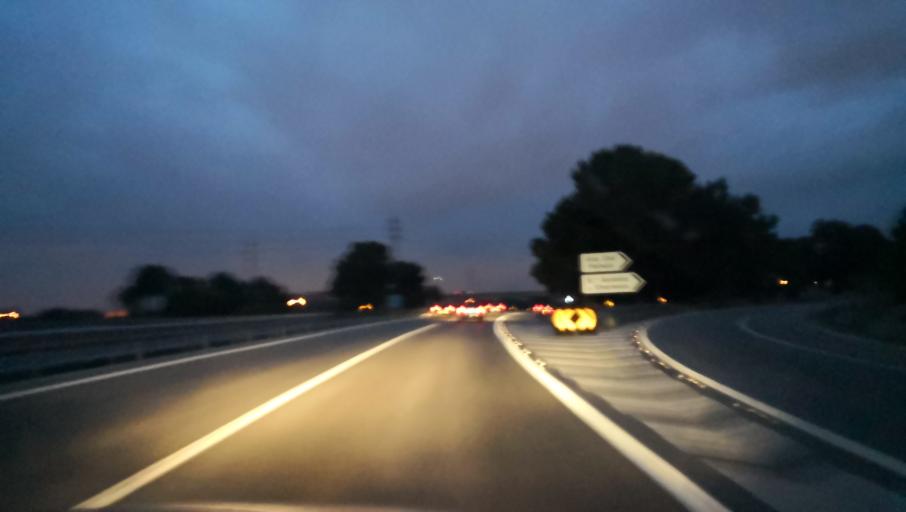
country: PT
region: Setubal
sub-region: Barreiro
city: Santo Antonio da Charneca
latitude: 38.6210
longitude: -9.0347
